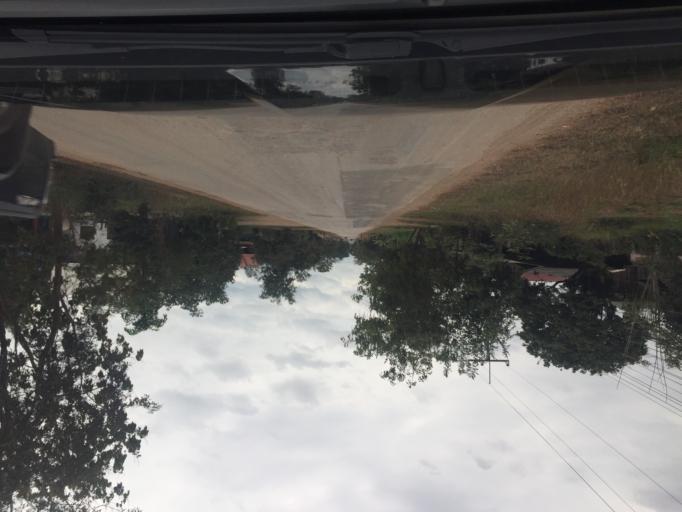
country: TH
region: Phayao
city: Pong
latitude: 19.1672
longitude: 100.3107
